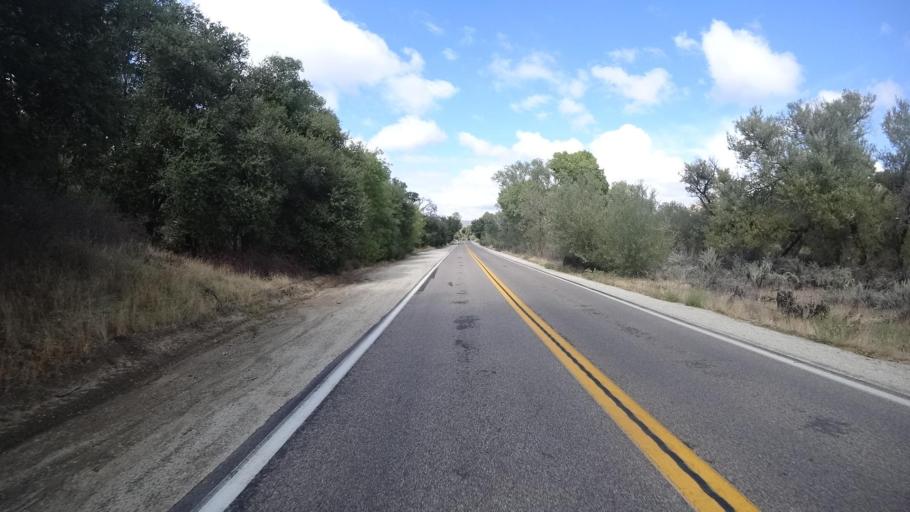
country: US
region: California
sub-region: San Diego County
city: Campo
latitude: 32.7045
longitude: -116.4901
